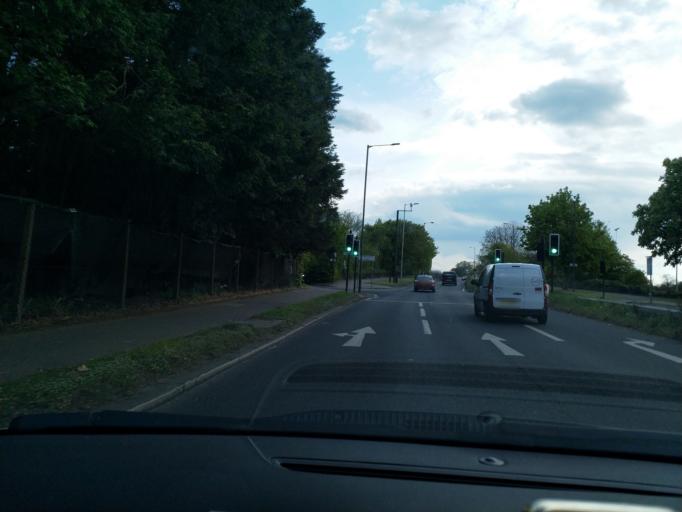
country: GB
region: England
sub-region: Greater London
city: Acton
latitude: 51.4750
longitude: -0.2667
